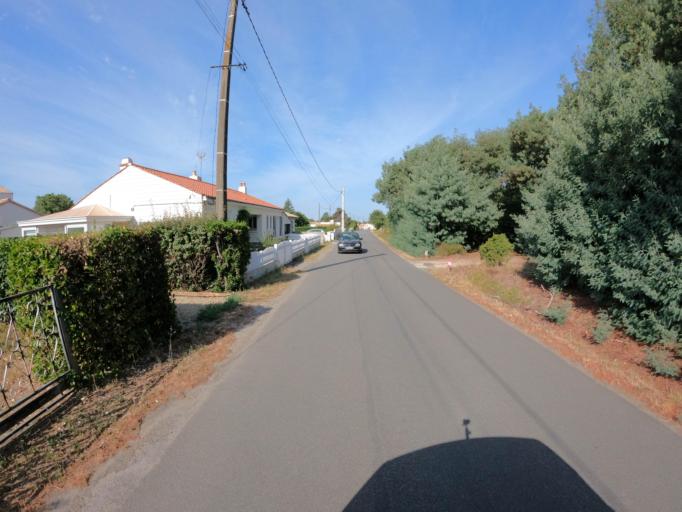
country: FR
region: Pays de la Loire
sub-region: Departement de la Vendee
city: Soullans
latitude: 46.8025
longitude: -1.9018
